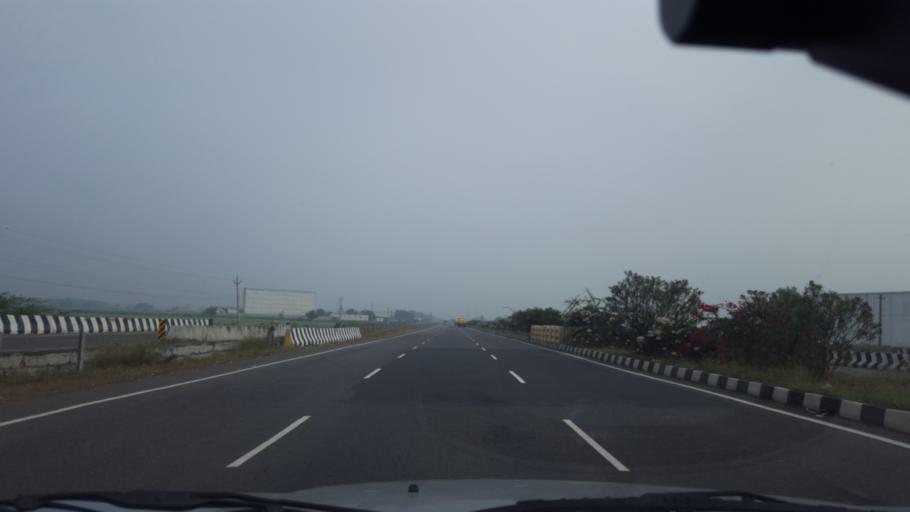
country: IN
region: Andhra Pradesh
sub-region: Guntur
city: Chilakalurupet
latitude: 16.0353
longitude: 80.1328
